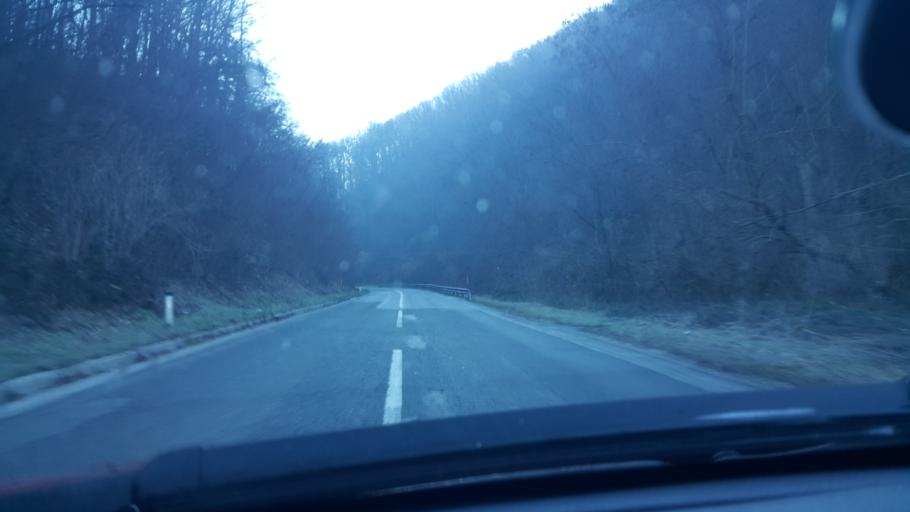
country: SI
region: Bistrica ob Sotli
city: Bistrica ob Sotli
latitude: 46.0486
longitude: 15.6744
